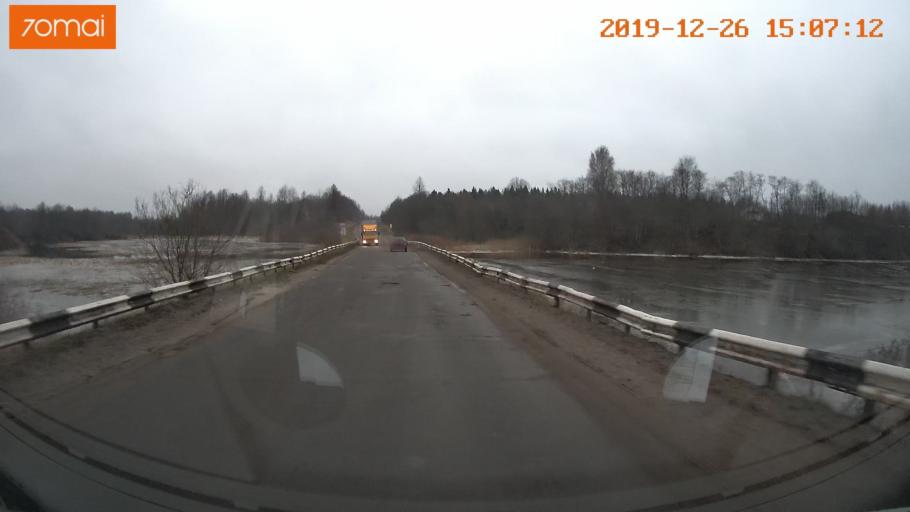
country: RU
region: Jaroslavl
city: Rybinsk
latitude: 58.1716
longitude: 38.8407
